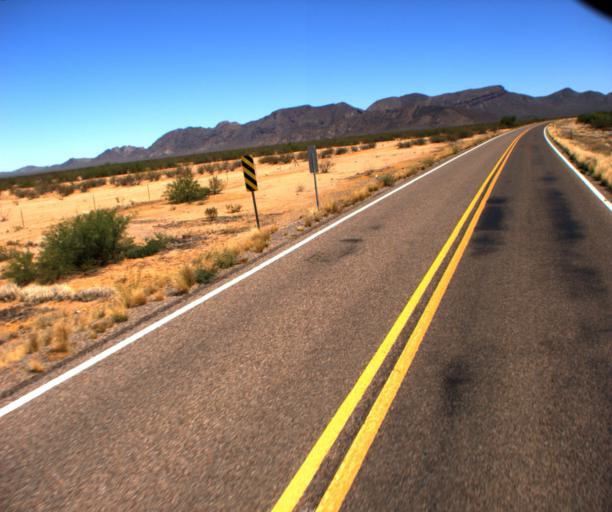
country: US
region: Arizona
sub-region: Yavapai County
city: Congress
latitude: 33.9797
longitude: -113.1400
